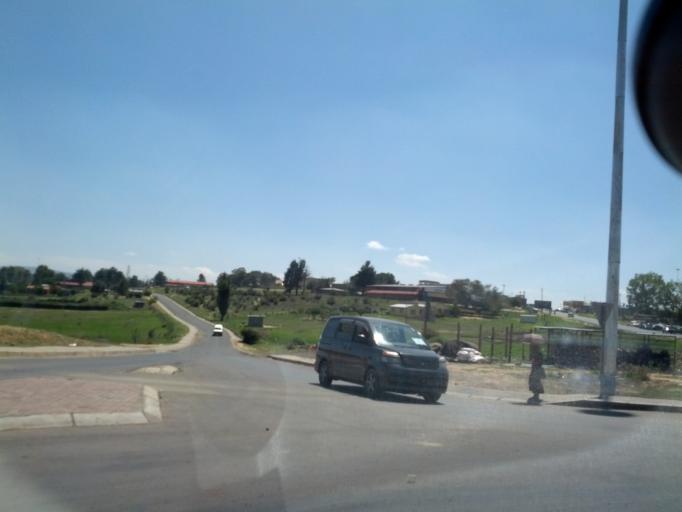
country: LS
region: Butha-Buthe
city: Butha-Buthe
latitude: -28.7716
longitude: 28.2451
